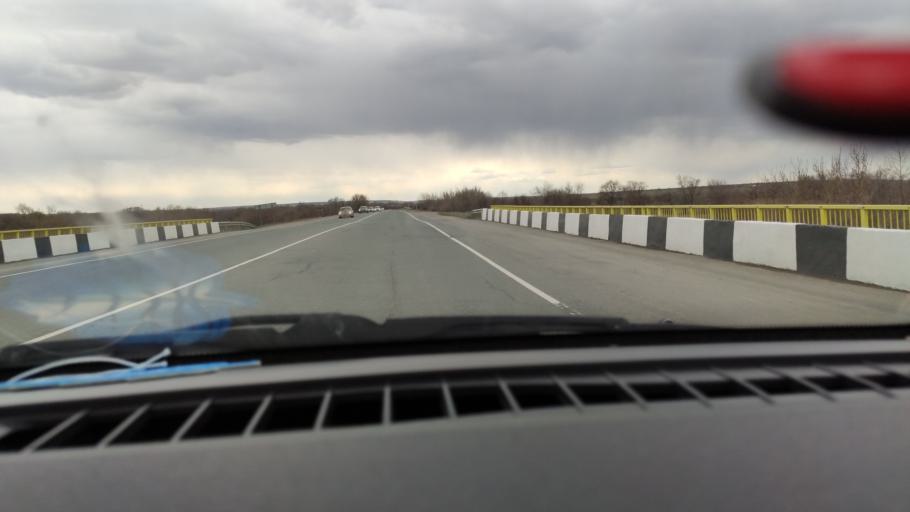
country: RU
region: Saratov
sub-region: Saratovskiy Rayon
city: Saratov
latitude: 51.7228
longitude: 46.0268
